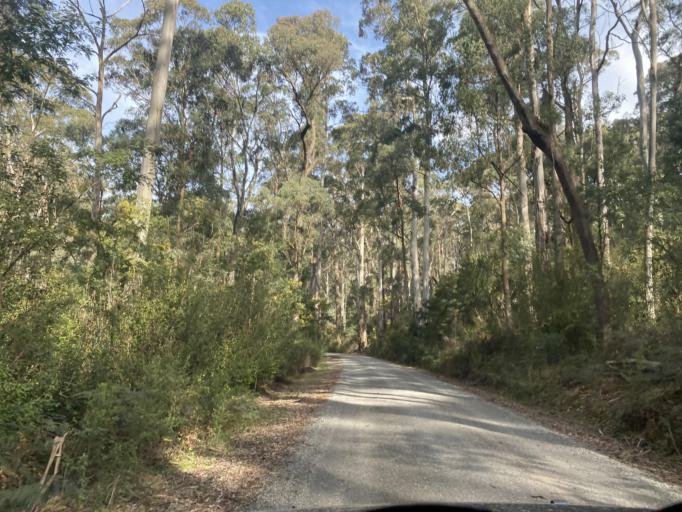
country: AU
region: Victoria
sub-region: Mansfield
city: Mansfield
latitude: -36.8617
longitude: 146.1951
